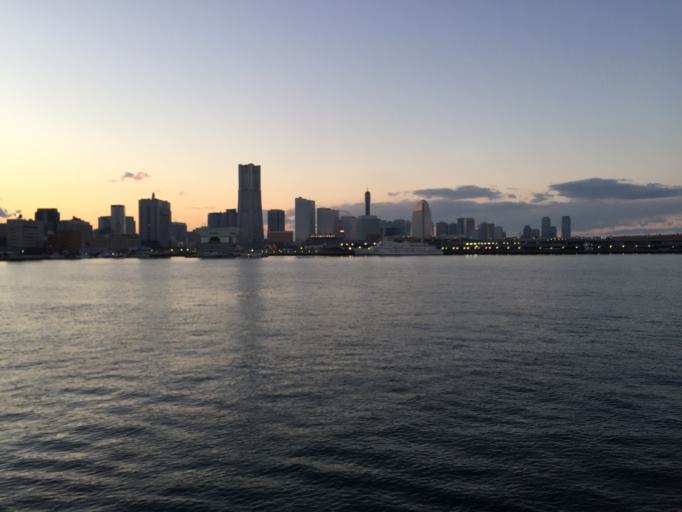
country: JP
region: Kanagawa
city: Yokohama
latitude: 35.4478
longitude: 139.6528
